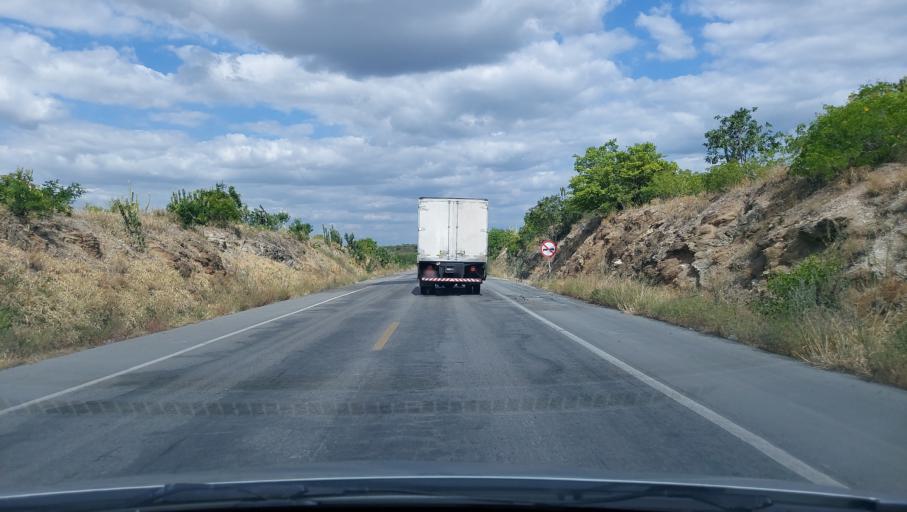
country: BR
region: Bahia
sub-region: Ipira
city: Ipira
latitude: -12.5001
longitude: -39.8591
